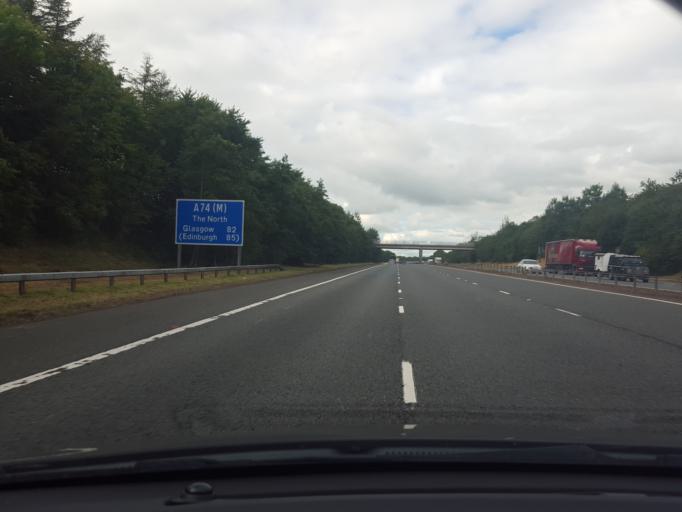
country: GB
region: Scotland
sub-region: Dumfries and Galloway
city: Gretna
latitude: 55.0285
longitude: -3.1455
